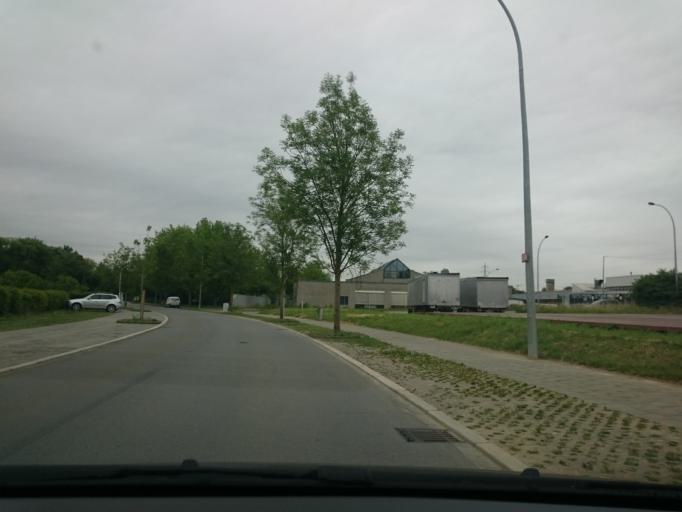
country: LU
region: Luxembourg
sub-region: Canton de Luxembourg
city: Luxembourg
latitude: 49.5993
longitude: 6.1014
